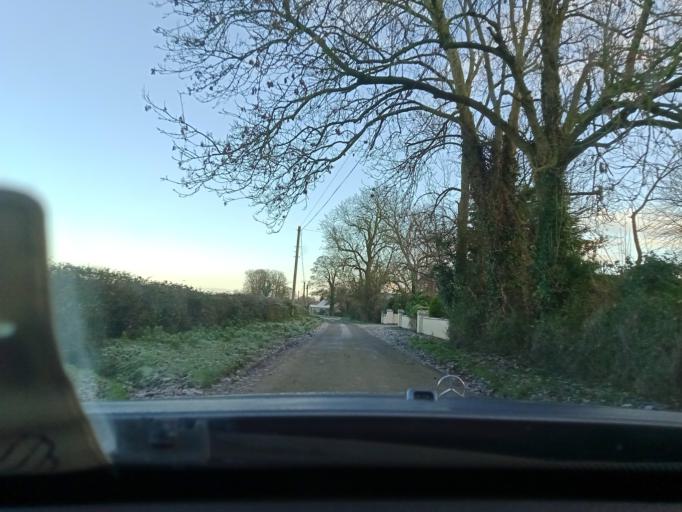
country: IE
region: Leinster
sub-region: County Carlow
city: Bagenalstown
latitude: 52.6397
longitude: -7.0241
